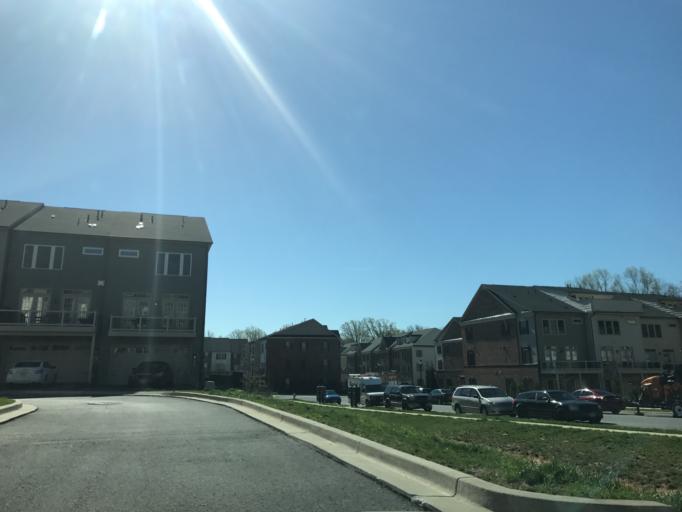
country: US
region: Maryland
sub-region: Anne Arundel County
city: Fort Meade
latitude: 39.1326
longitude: -76.7469
